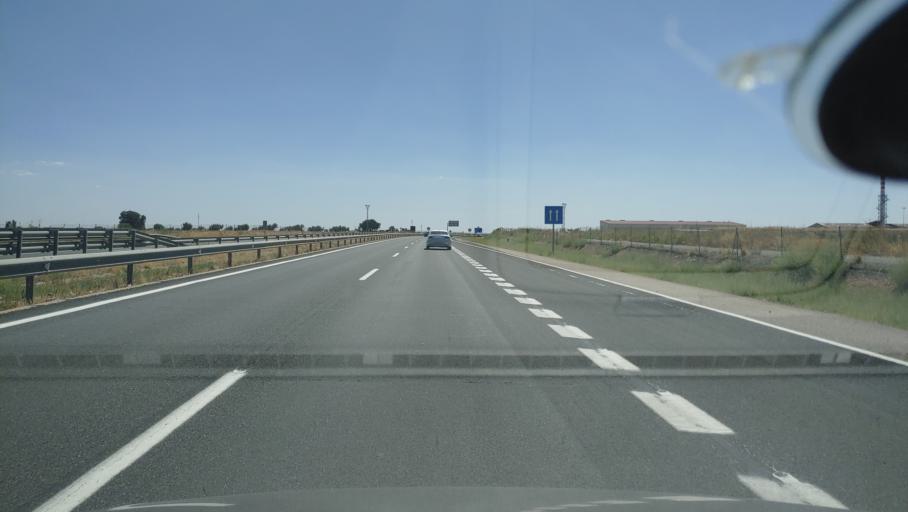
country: ES
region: Castille-La Mancha
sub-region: Provincia de Ciudad Real
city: Villarta de San Juan
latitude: 39.2315
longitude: -3.4115
